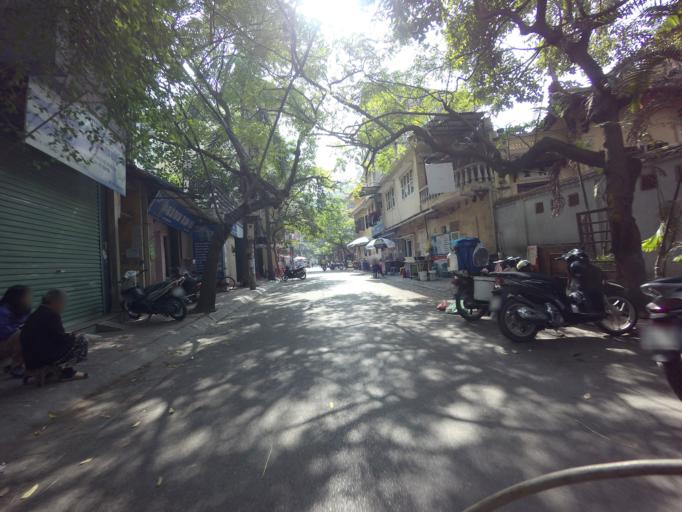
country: VN
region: Ha Noi
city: Hoan Kiem
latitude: 21.0464
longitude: 105.8409
